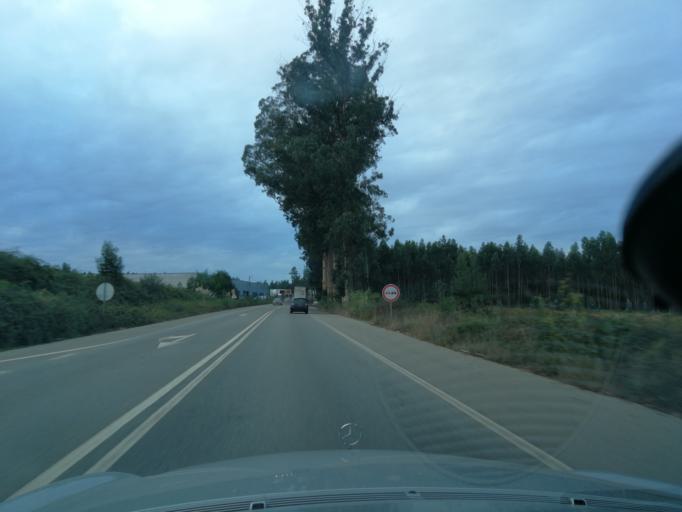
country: PT
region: Aveiro
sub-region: Albergaria-A-Velha
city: Albergaria-a-Velha
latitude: 40.6636
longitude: -8.4754
